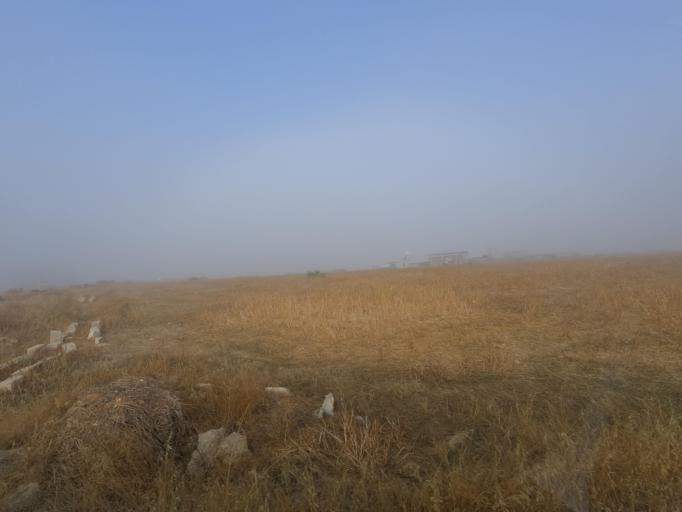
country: CY
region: Ammochostos
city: Acheritou
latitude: 35.0938
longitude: 33.8826
